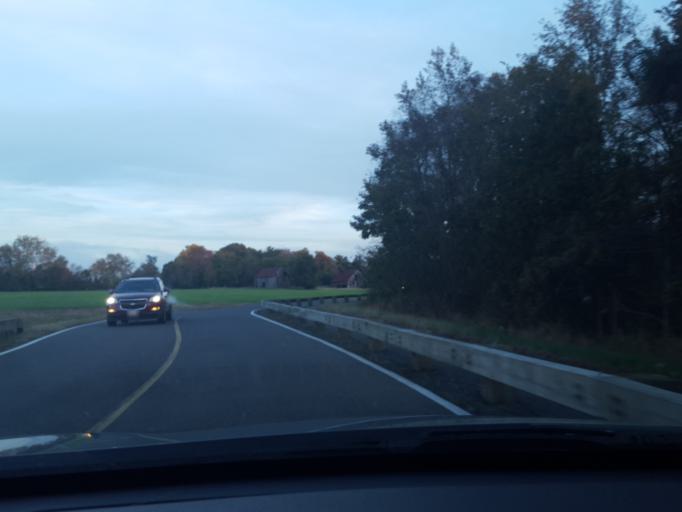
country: US
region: Maryland
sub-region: Prince George's County
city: Kettering
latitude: 38.8829
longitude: -76.7894
